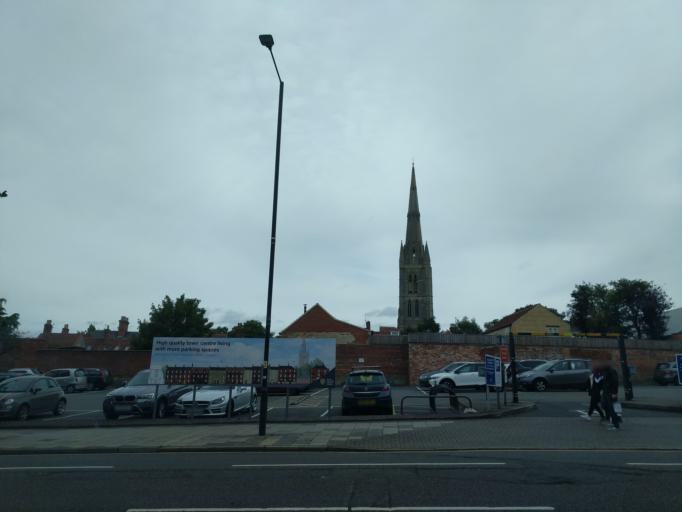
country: GB
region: England
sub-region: Lincolnshire
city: Grantham
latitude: 52.9143
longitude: -0.6439
